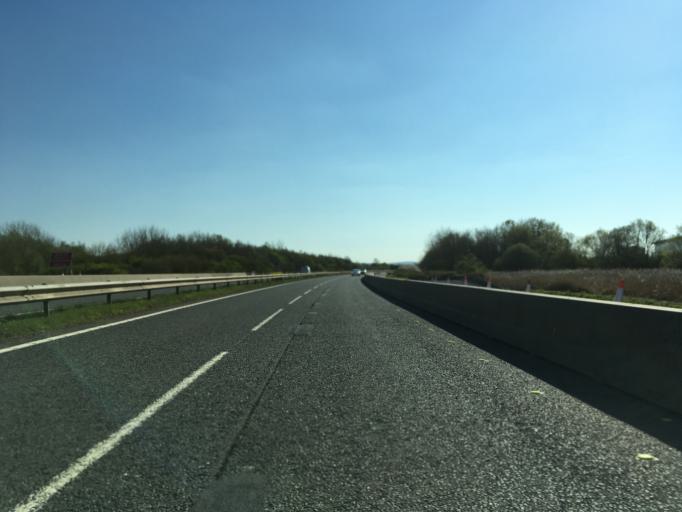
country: GB
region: England
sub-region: South Gloucestershire
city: Severn Beach
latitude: 51.5385
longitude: -2.6391
